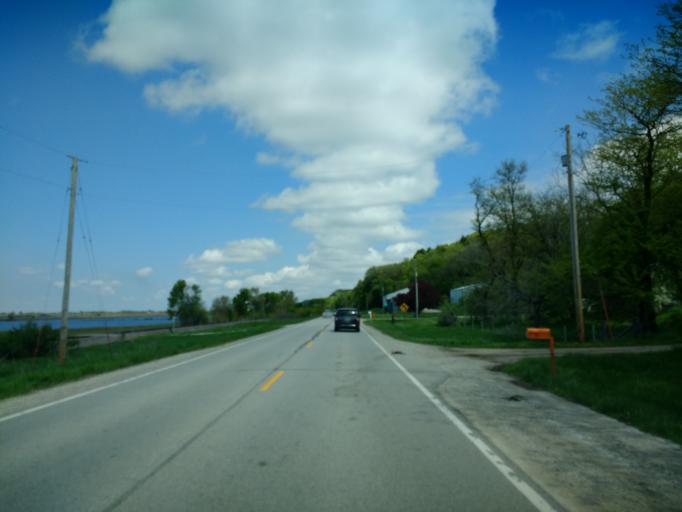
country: US
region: Iowa
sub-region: Harrison County
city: Missouri Valley
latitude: 41.4404
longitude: -95.8700
